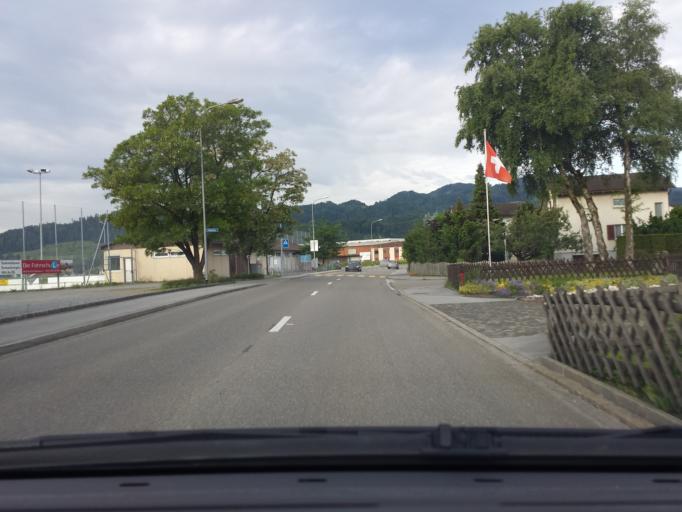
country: CH
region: Saint Gallen
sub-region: Wahlkreis Rheintal
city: Au
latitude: 47.4293
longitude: 9.6309
